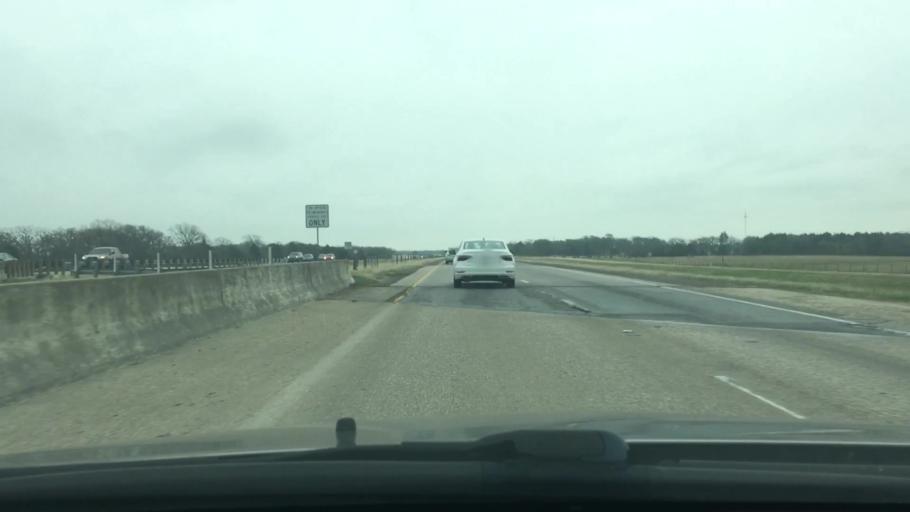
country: US
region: Texas
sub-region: Freestone County
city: Fairfield
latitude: 31.7718
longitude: -96.2222
